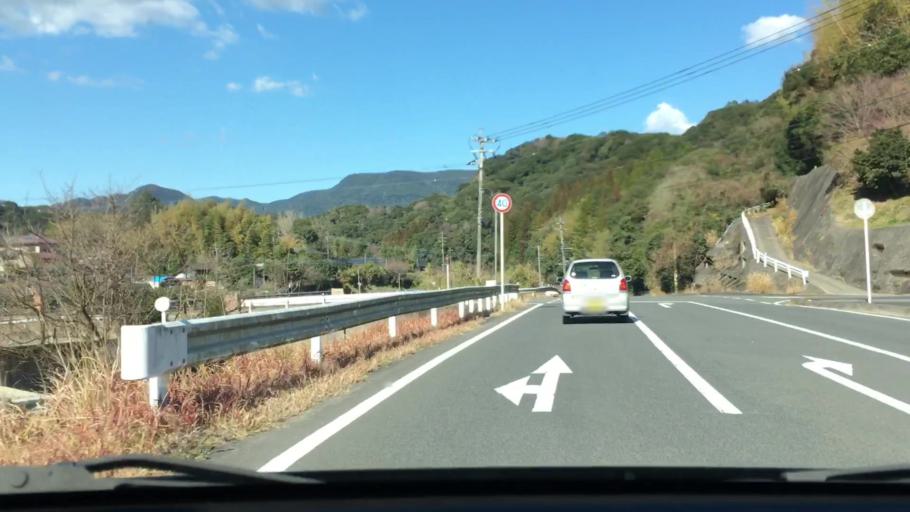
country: JP
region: Kagoshima
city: Ijuin
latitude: 31.6943
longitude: 130.4618
